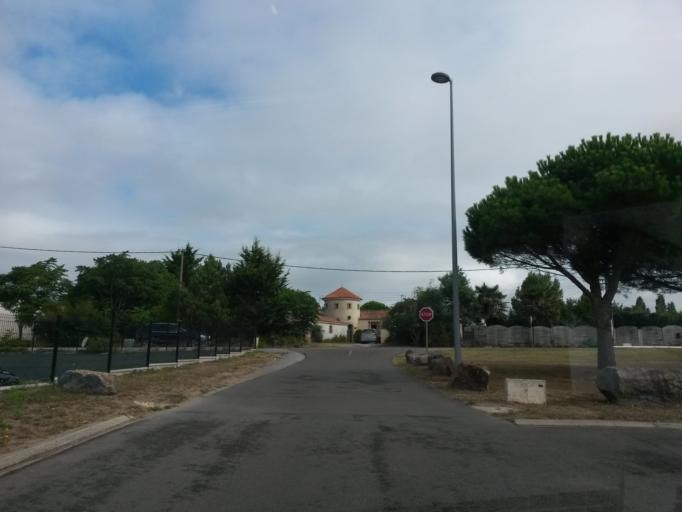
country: FR
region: Pays de la Loire
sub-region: Departement de la Vendee
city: Olonne-sur-Mer
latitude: 46.5228
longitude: -1.7845
